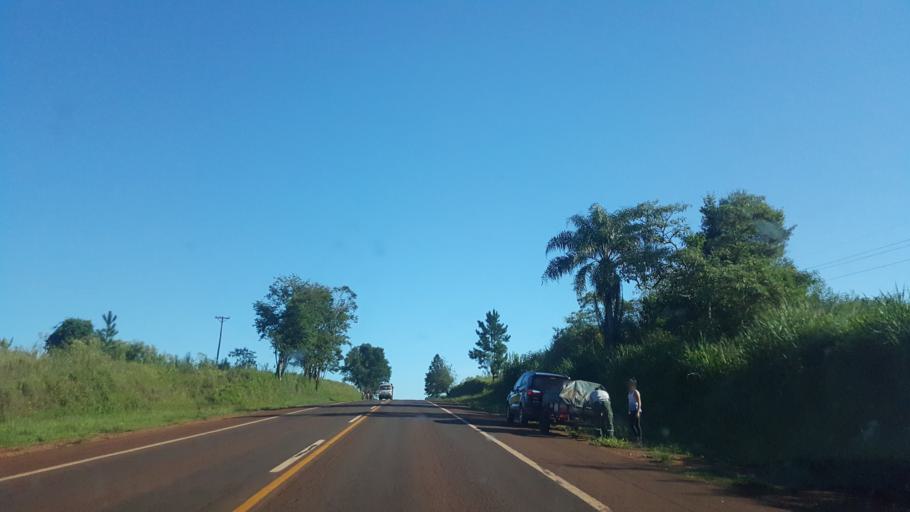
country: AR
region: Misiones
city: Puerto Esperanza
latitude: -26.1449
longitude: -54.5826
